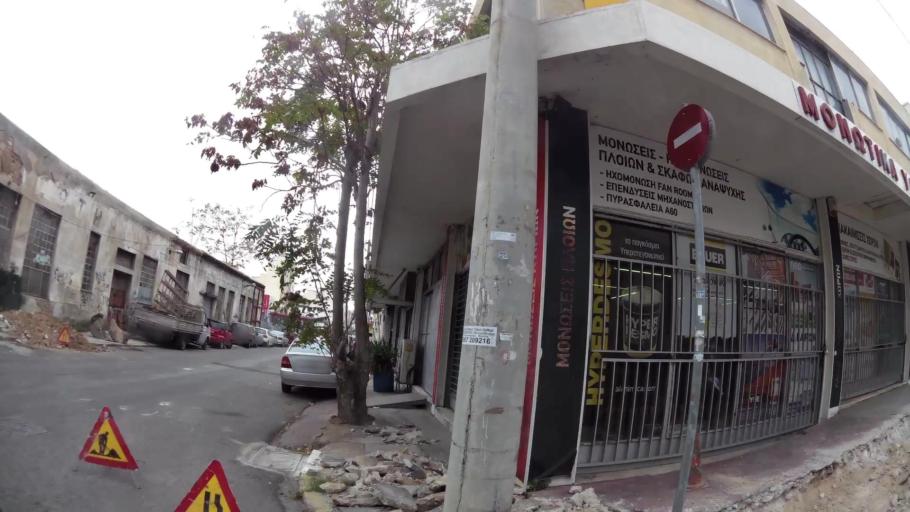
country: GR
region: Attica
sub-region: Nomos Attikis
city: Piraeus
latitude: 37.9521
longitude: 23.6411
